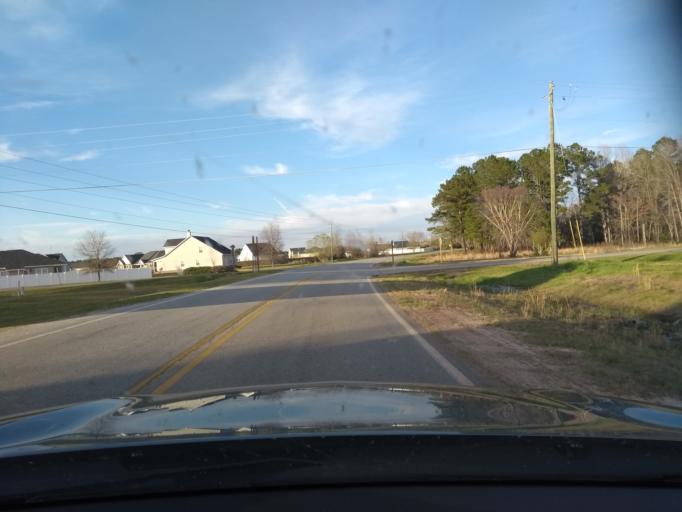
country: US
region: Georgia
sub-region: Bulloch County
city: Statesboro
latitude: 32.3593
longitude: -81.7708
